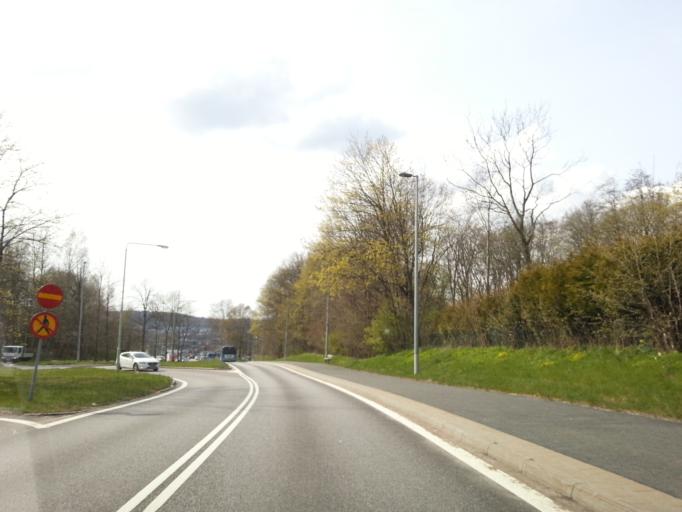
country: SE
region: Vaestra Goetaland
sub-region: Goteborg
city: Gardsten
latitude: 57.7892
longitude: 12.0203
